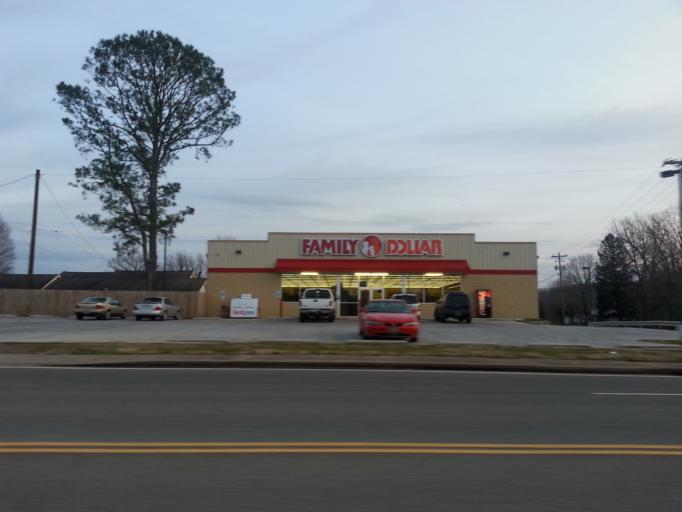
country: US
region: Tennessee
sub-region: McMinn County
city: Englewood
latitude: 35.4271
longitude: -84.4827
